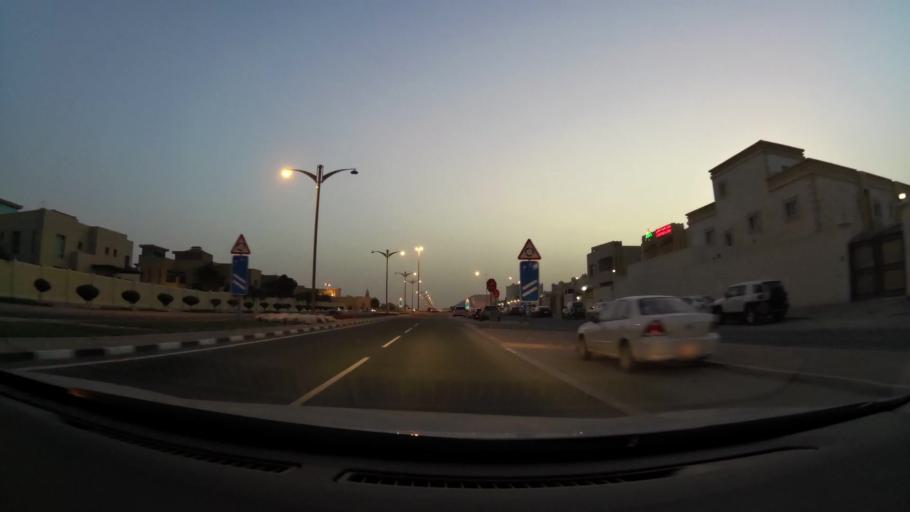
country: QA
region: Baladiyat ar Rayyan
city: Ar Rayyan
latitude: 25.2609
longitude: 51.4683
